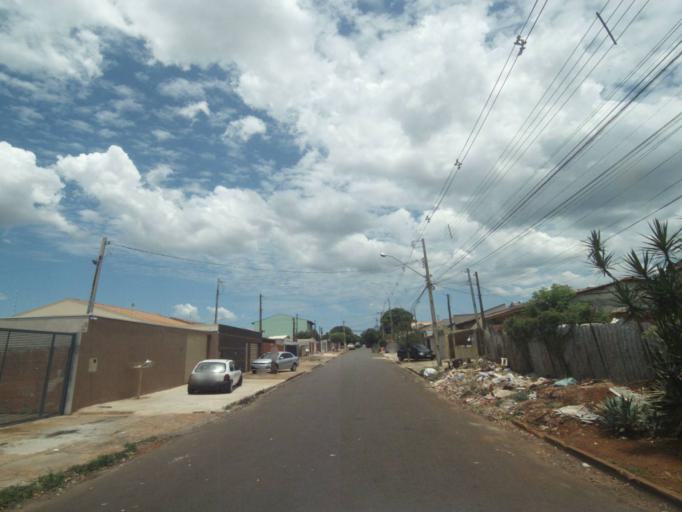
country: BR
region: Parana
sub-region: Londrina
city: Londrina
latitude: -23.3077
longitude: -51.2198
